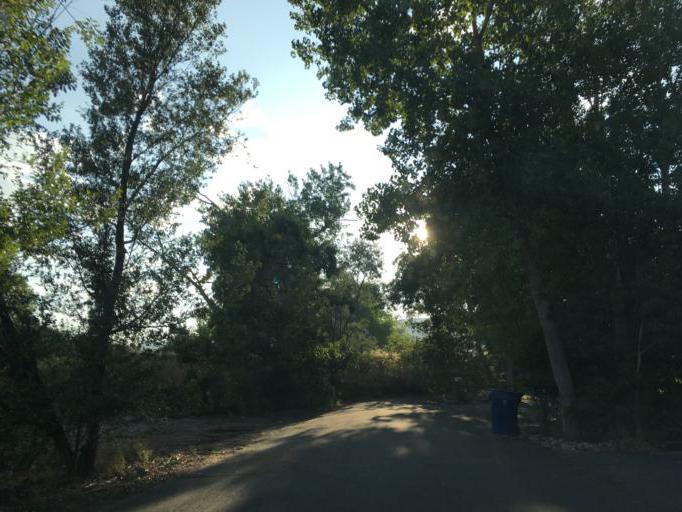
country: US
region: Colorado
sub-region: Jefferson County
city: Applewood
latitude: 39.7853
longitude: -105.1676
